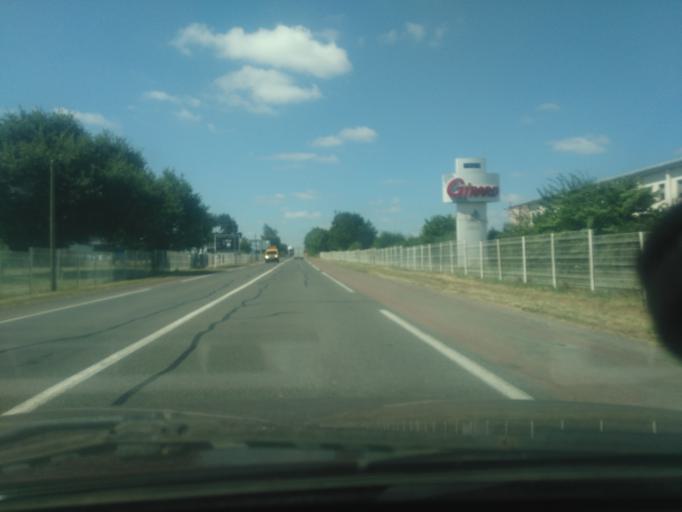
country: FR
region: Pays de la Loire
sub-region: Departement de la Vendee
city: Les Essarts
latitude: 46.7589
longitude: -1.2472
